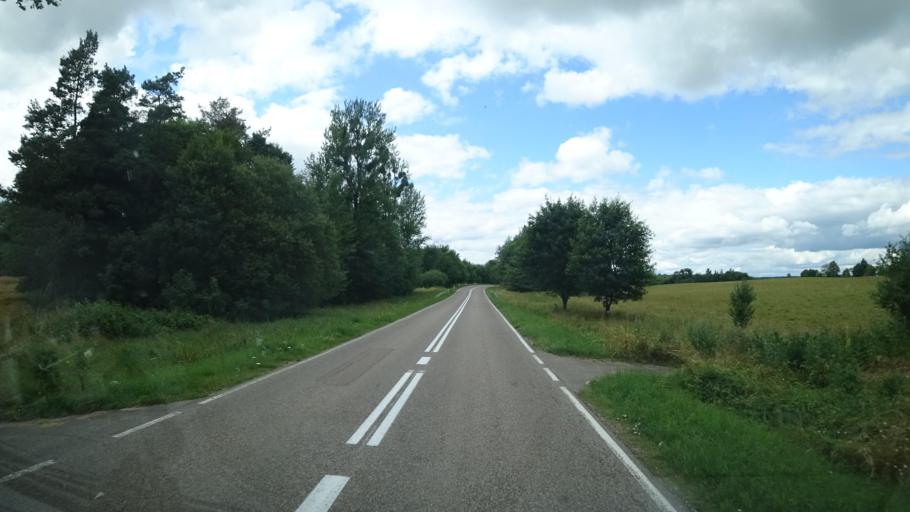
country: PL
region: Warmian-Masurian Voivodeship
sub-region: Powiat goldapski
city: Banie Mazurskie
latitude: 54.2106
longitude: 22.1799
